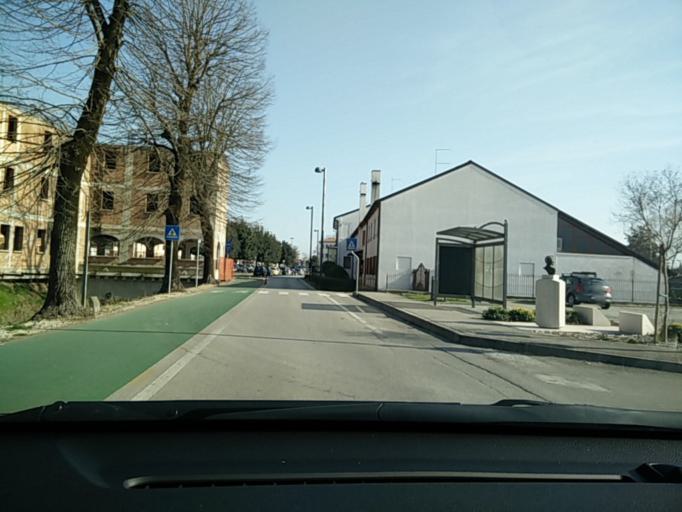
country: IT
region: Veneto
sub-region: Provincia di Venezia
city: Meolo
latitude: 45.6192
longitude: 12.4524
